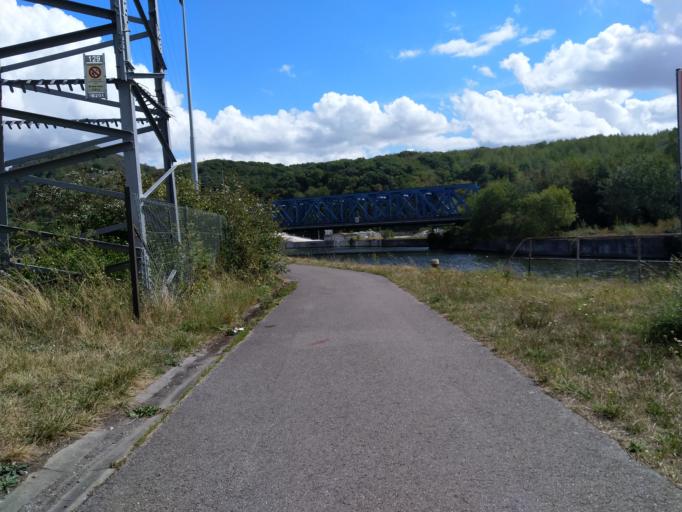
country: BE
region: Wallonia
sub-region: Province du Hainaut
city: Charleroi
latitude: 50.3963
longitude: 4.4845
